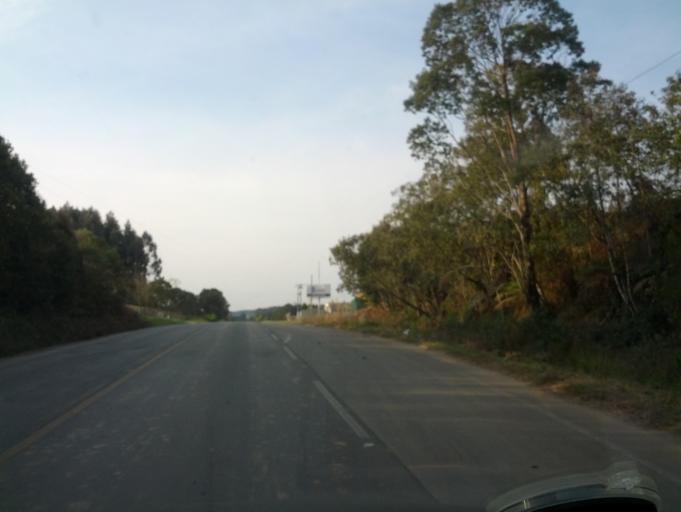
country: BR
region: Santa Catarina
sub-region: Otacilio Costa
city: Otacilio Costa
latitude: -27.6003
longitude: -50.1721
